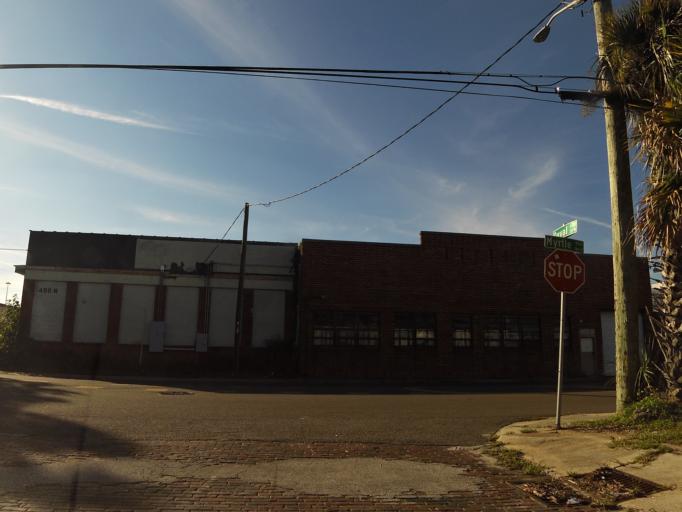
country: US
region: Florida
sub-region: Duval County
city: Jacksonville
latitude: 30.3330
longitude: -81.6758
